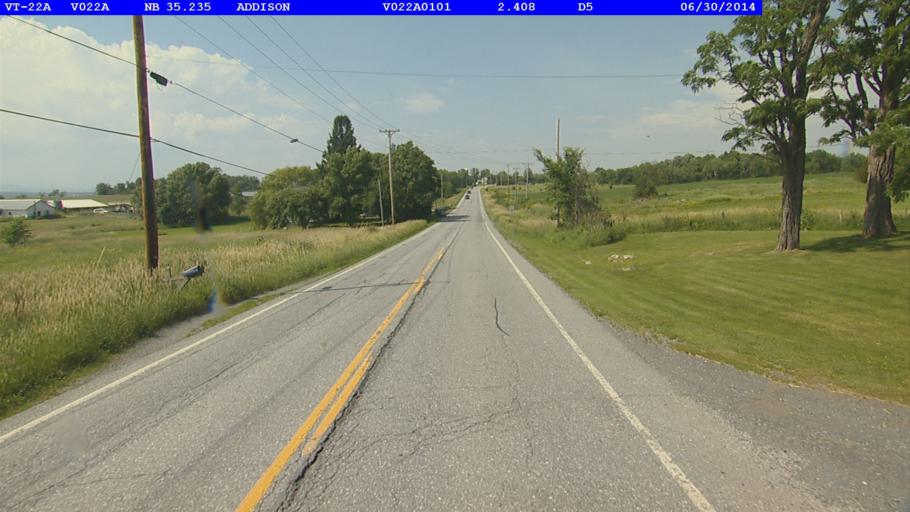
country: US
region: Vermont
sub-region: Addison County
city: Vergennes
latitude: 44.0642
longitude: -73.3035
